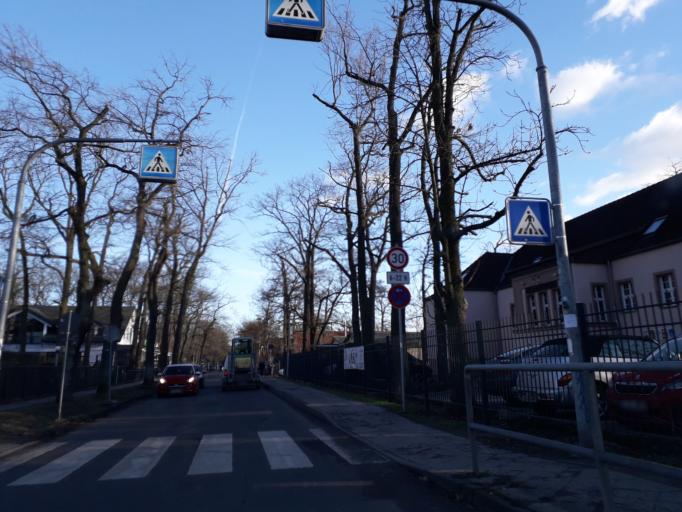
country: DE
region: Brandenburg
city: Brieselang
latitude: 52.5807
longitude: 12.9992
